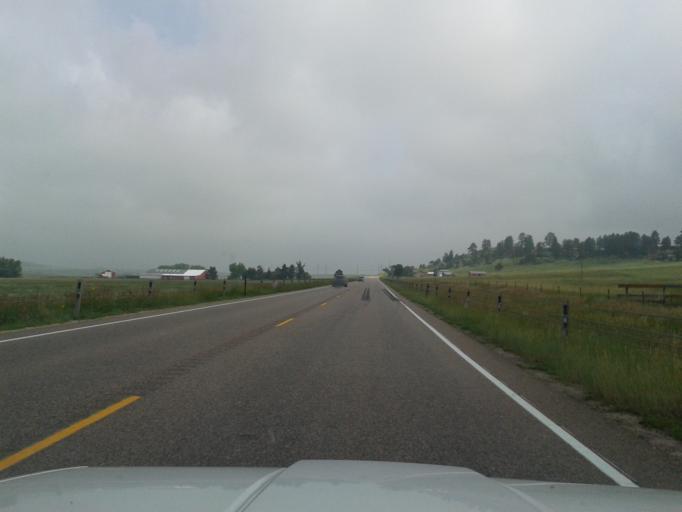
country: US
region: Colorado
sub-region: Elbert County
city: Elizabeth
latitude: 39.2538
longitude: -104.7011
